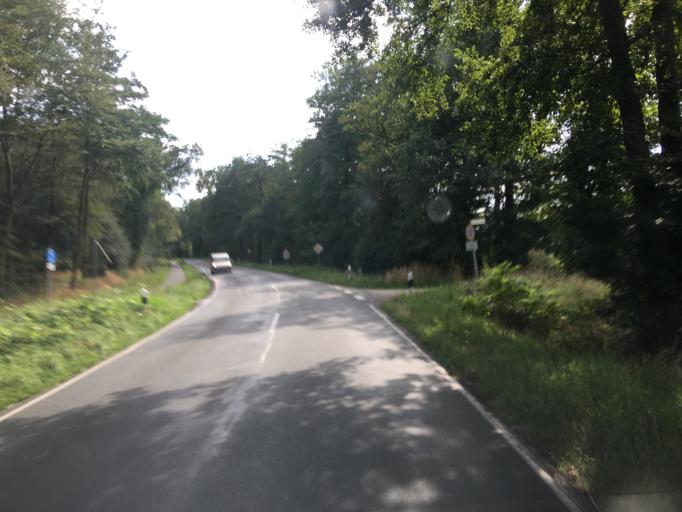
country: DE
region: Lower Saxony
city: Friesoythe
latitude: 53.0467
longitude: 7.8566
